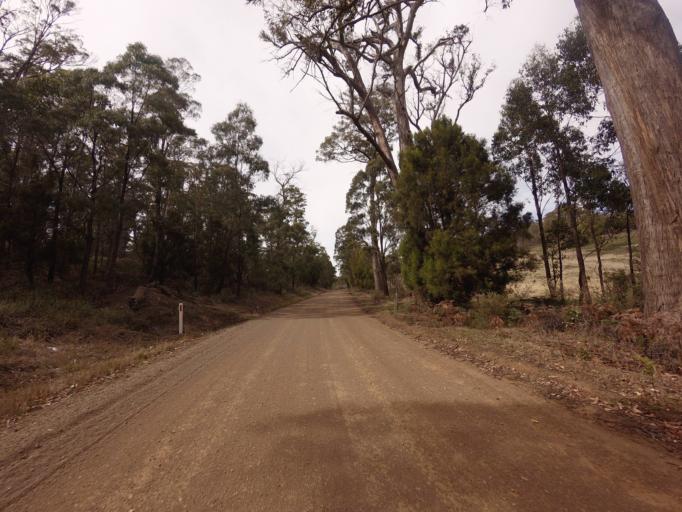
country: AU
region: Tasmania
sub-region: Sorell
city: Sorell
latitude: -42.4838
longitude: 147.6164
